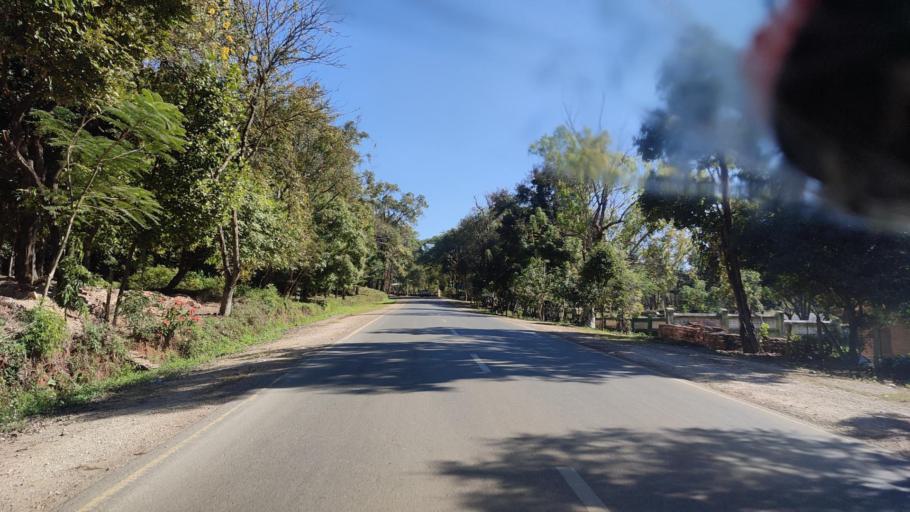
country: MM
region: Mandalay
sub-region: Pyin Oo Lwin District
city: Pyin Oo Lwin
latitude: 21.9939
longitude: 96.4246
